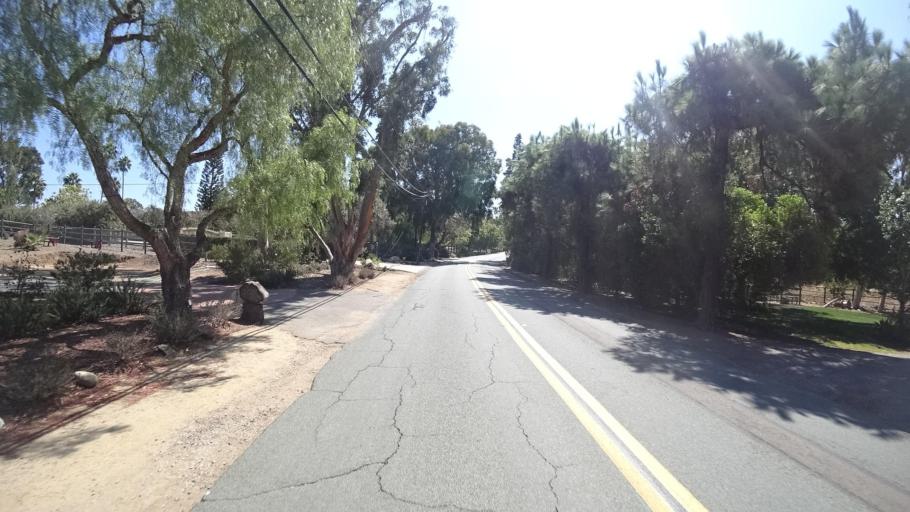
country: US
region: California
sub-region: San Diego County
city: Rancho Santa Fe
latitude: 33.0292
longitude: -117.1890
